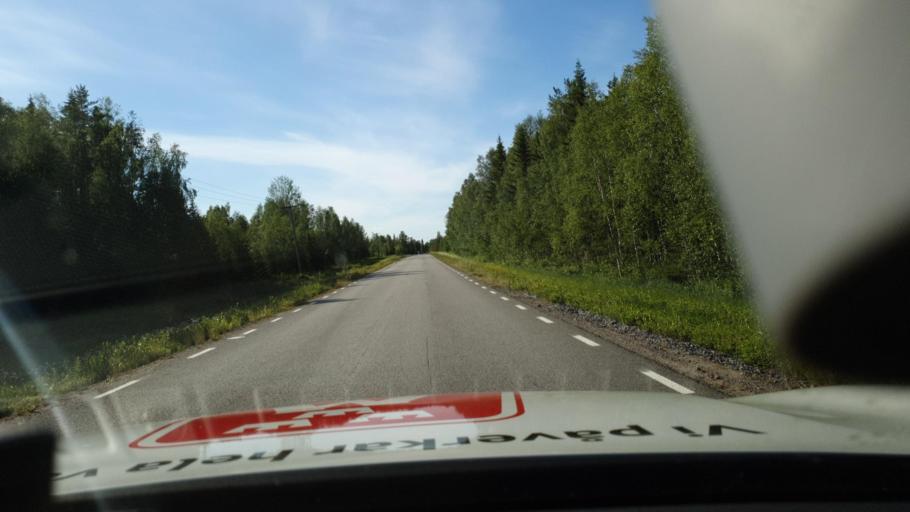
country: SE
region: Norrbotten
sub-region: Kalix Kommun
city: Toere
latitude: 65.8989
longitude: 22.6193
